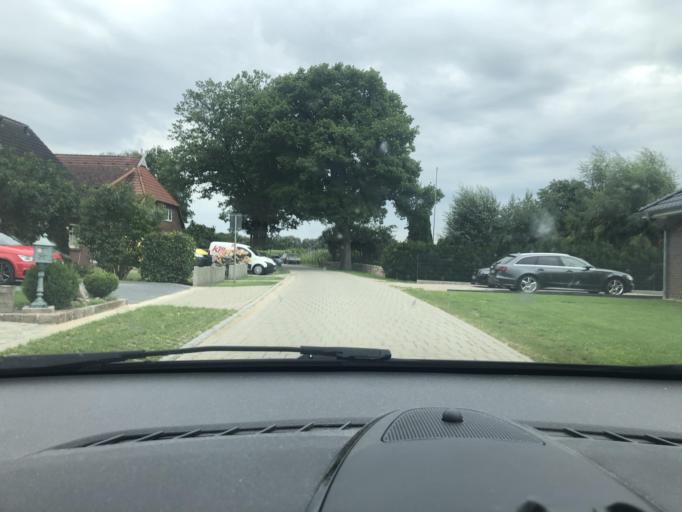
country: DE
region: Mecklenburg-Vorpommern
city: Nostorf
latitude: 53.3538
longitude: 10.6653
